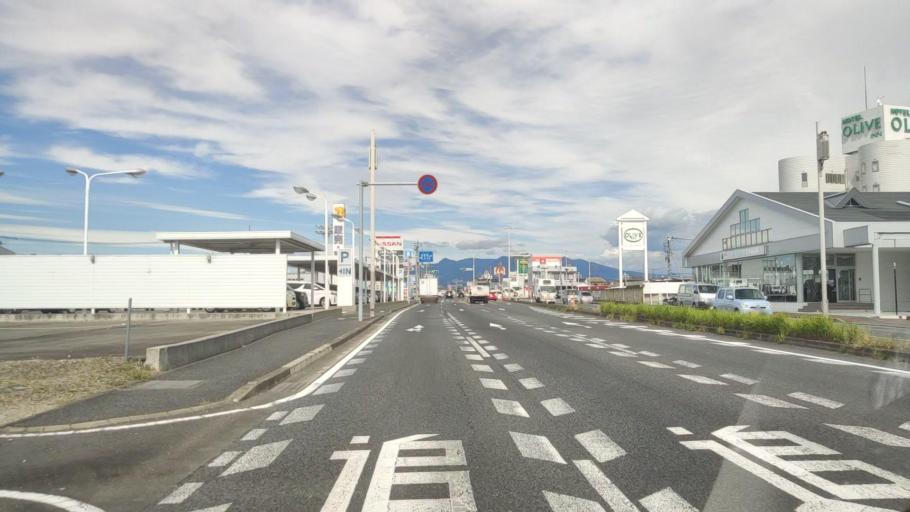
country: JP
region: Gunma
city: Takasaki
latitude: 36.3637
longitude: 139.0190
